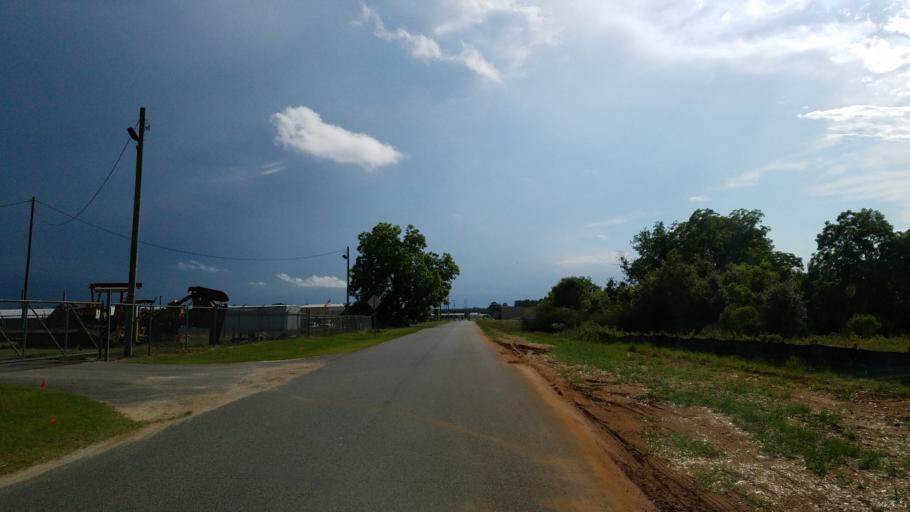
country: US
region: Georgia
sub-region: Tift County
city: Tifton
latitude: 31.4486
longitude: -83.5395
